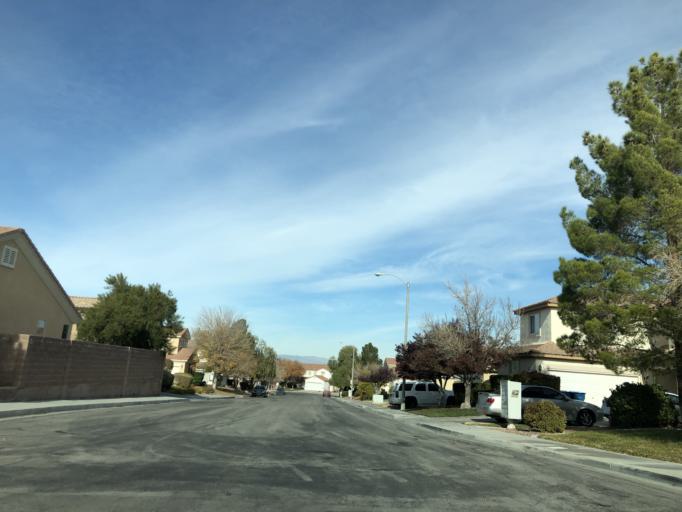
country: US
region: Nevada
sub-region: Clark County
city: Whitney
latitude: 36.0075
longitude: -115.0914
